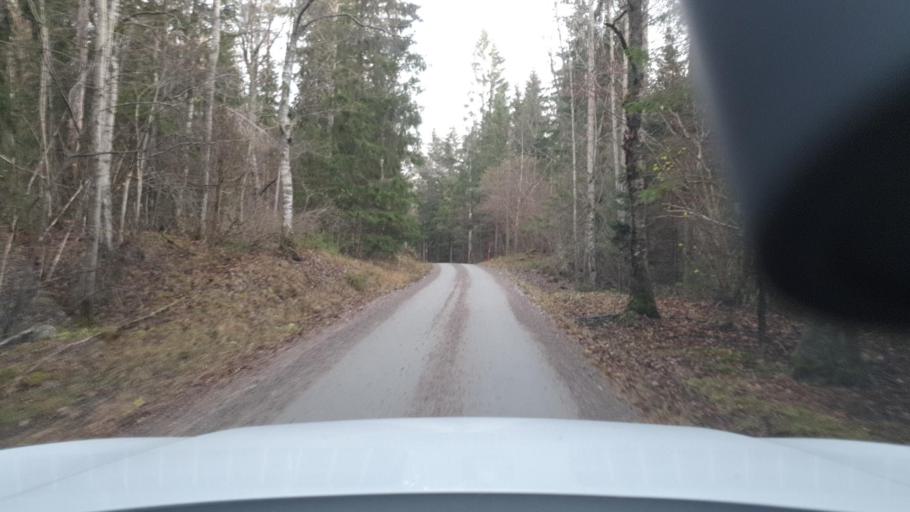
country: SE
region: Uppsala
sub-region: Tierps Kommun
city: Karlholmsbruk
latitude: 60.5031
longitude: 17.5389
